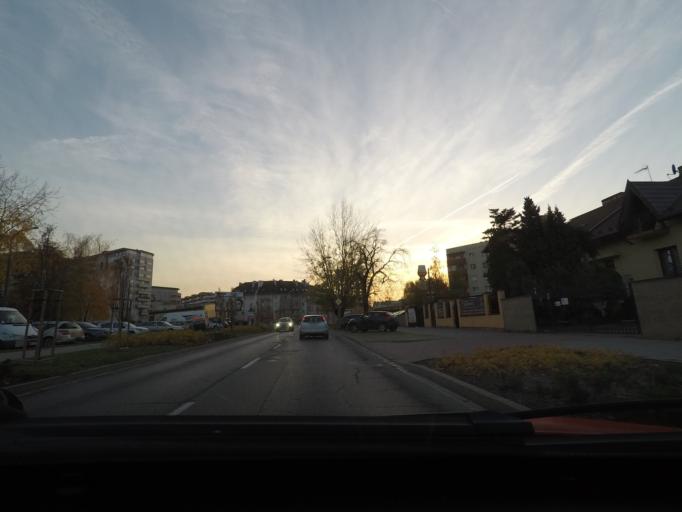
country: PL
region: Lesser Poland Voivodeship
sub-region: Krakow
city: Krakow
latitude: 50.0297
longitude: 19.9188
